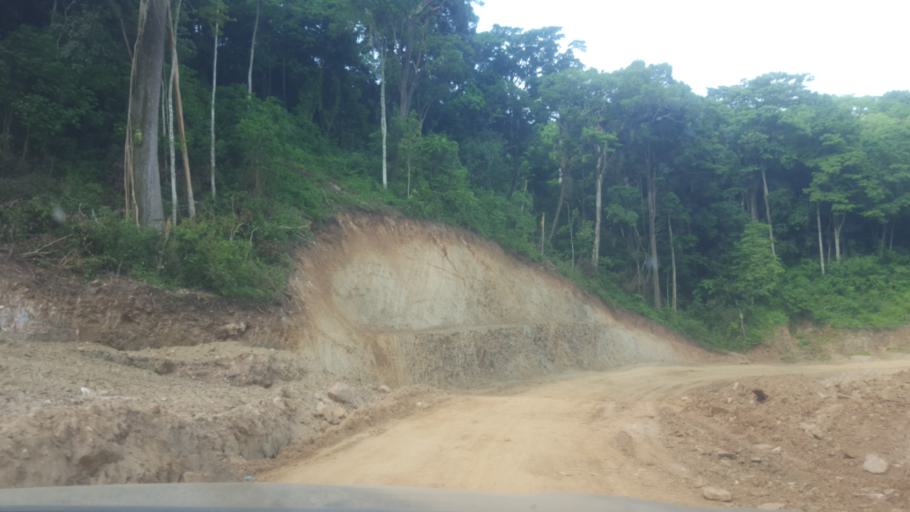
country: ET
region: Southern Nations, Nationalities, and People's Region
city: Tippi
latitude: 7.5411
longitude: 34.9766
